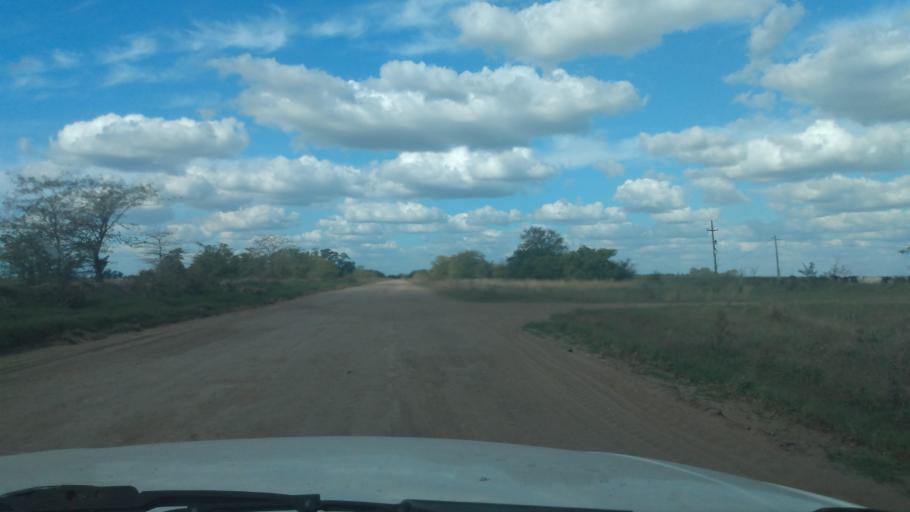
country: AR
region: Buenos Aires
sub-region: Partido de Navarro
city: Navarro
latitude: -35.0123
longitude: -59.4856
